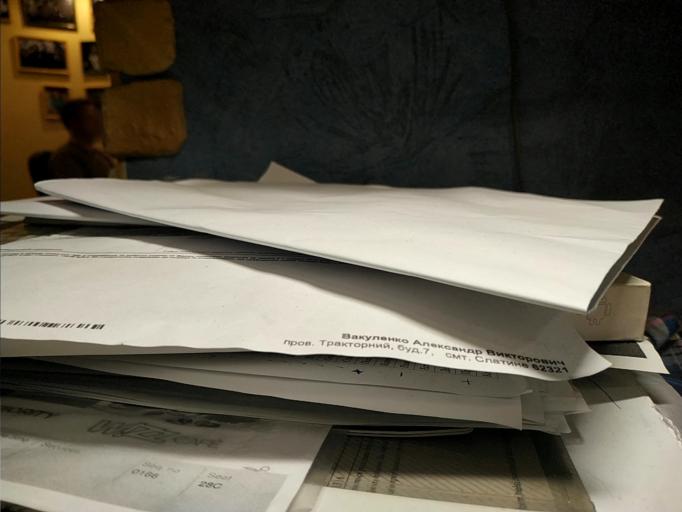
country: RU
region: Tverskaya
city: Zubtsov
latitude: 56.1314
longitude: 34.5091
